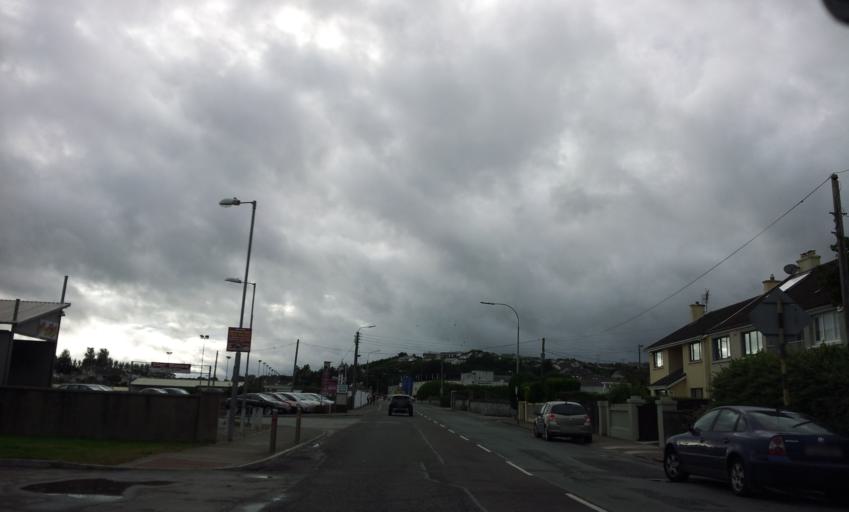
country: IE
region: Munster
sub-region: County Cork
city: Youghal
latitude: 51.9408
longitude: -7.8539
